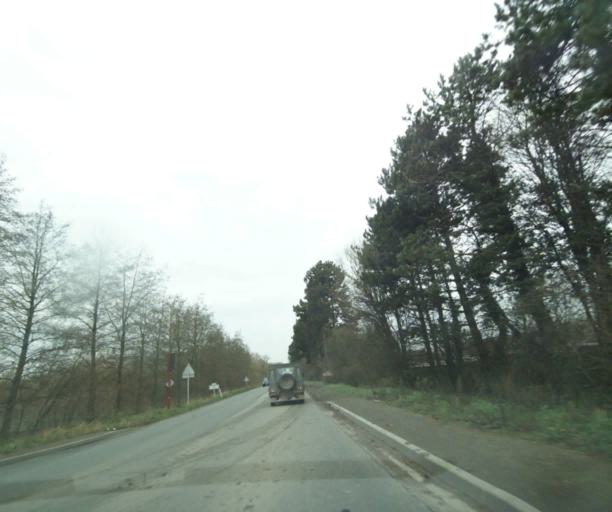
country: FR
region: Nord-Pas-de-Calais
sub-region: Departement du Nord
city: Vicq
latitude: 50.4051
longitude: 3.5947
